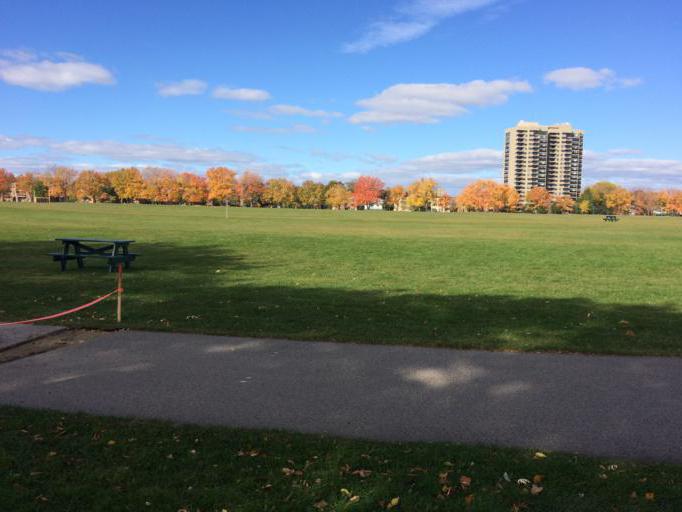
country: CA
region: Quebec
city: Quebec
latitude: 46.7962
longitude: -71.2277
